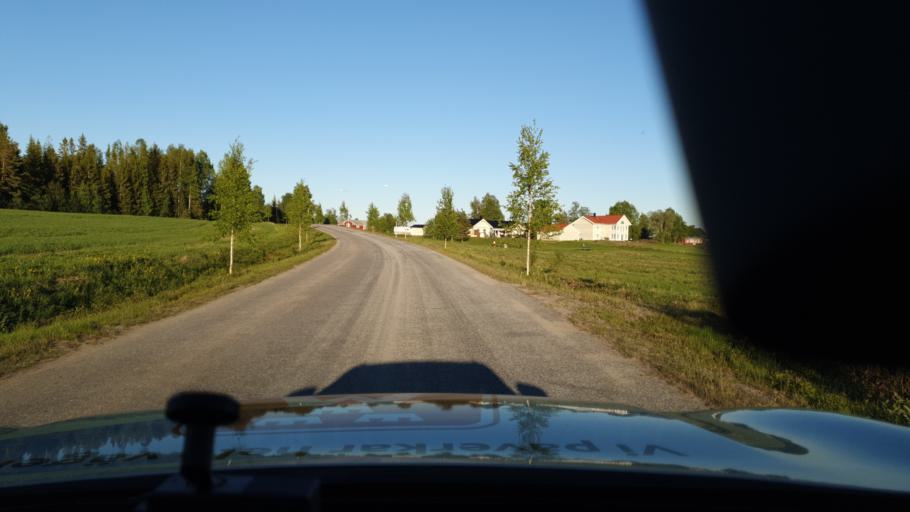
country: SE
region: Vaesterbotten
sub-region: Umea Kommun
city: Roback
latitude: 64.0154
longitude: 20.1170
